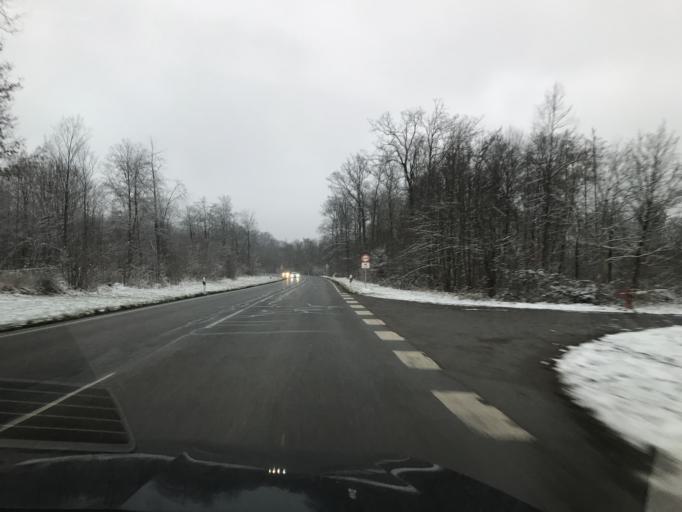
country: DE
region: Baden-Wuerttemberg
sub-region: Regierungsbezirk Stuttgart
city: Altbach
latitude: 48.7365
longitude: 9.3971
